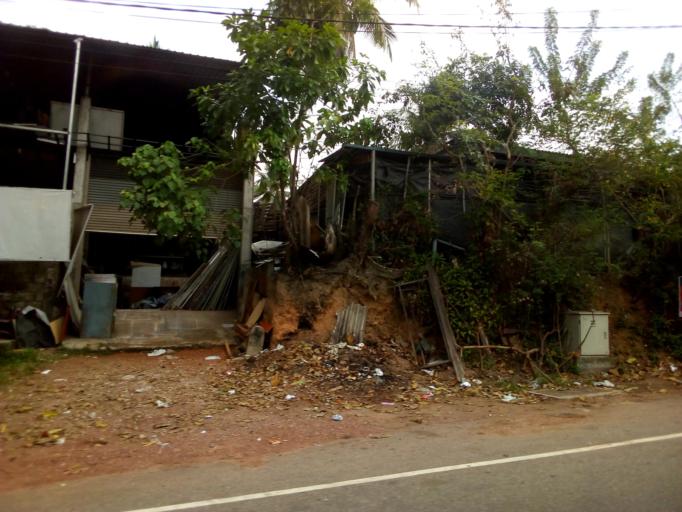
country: LK
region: Western
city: Maharagama
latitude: 6.8433
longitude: 79.9597
